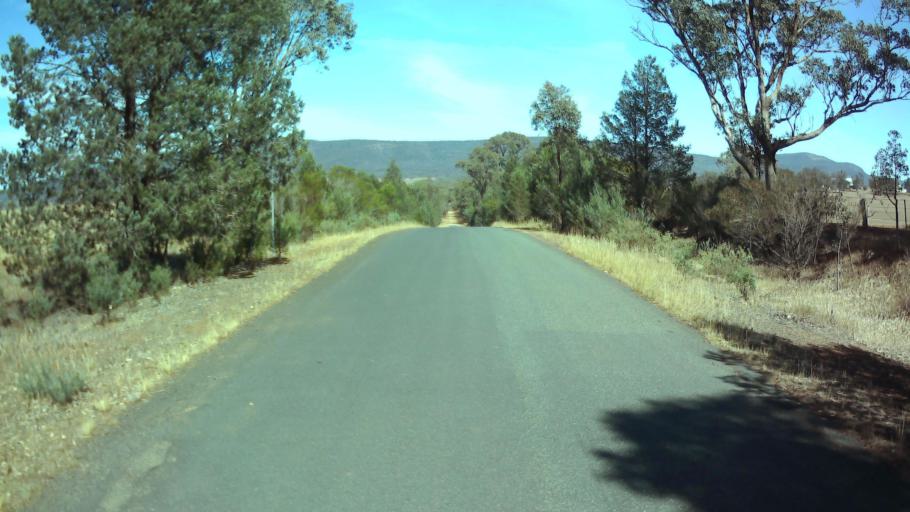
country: AU
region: New South Wales
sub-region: Weddin
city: Grenfell
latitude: -33.9412
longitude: 148.0655
